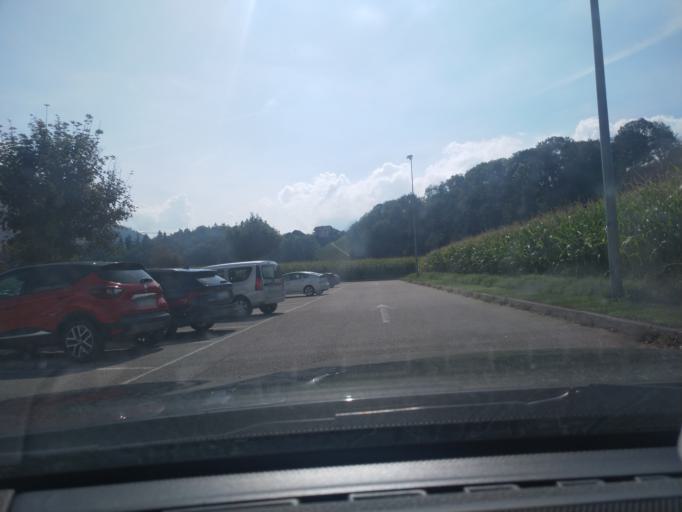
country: CH
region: Fribourg
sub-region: Gruyere District
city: Broc
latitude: 46.6081
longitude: 7.1041
